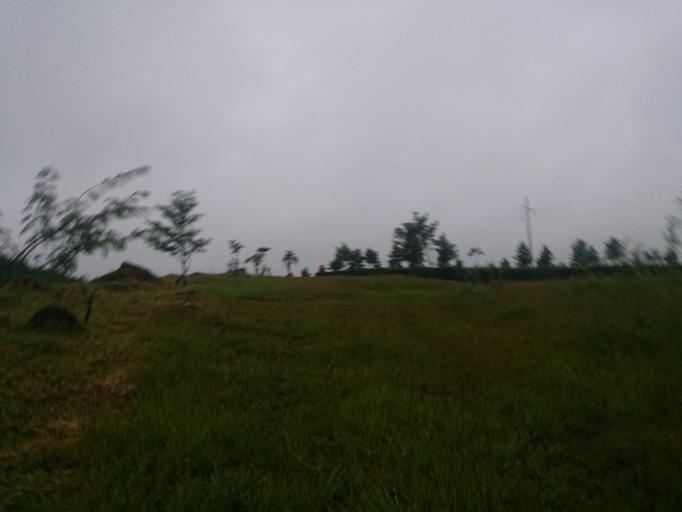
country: AR
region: Misiones
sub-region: Departamento de Obera
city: Obera
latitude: -27.4413
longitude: -55.0828
